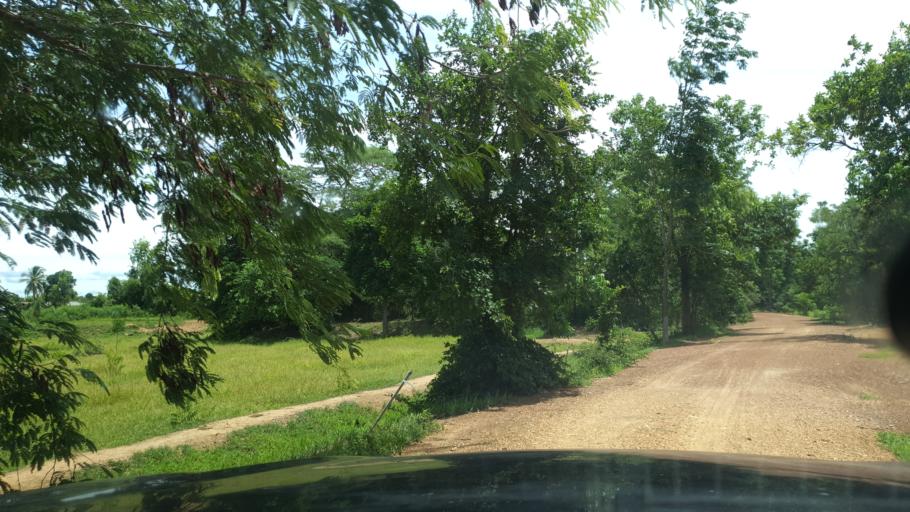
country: TH
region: Sukhothai
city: Ban Na
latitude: 17.0841
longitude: 99.6900
